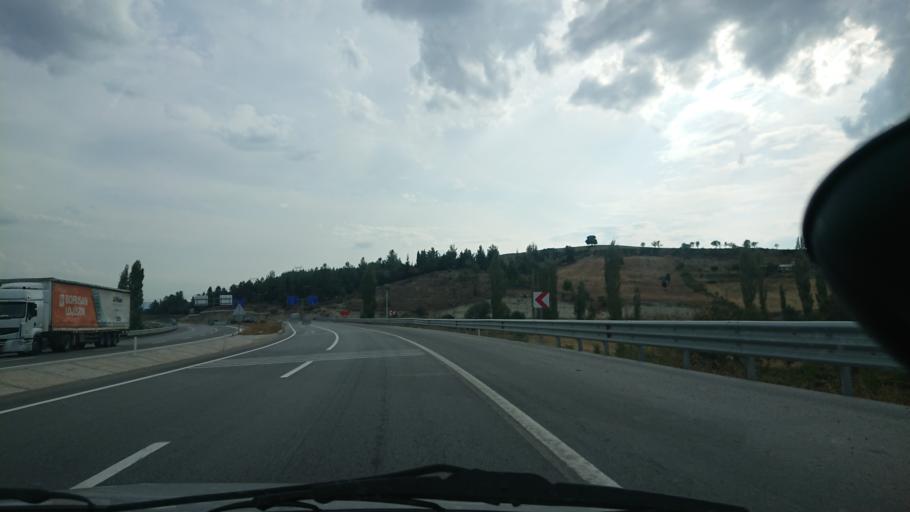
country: TR
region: Kuetahya
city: Gediz
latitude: 39.0333
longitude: 29.4170
